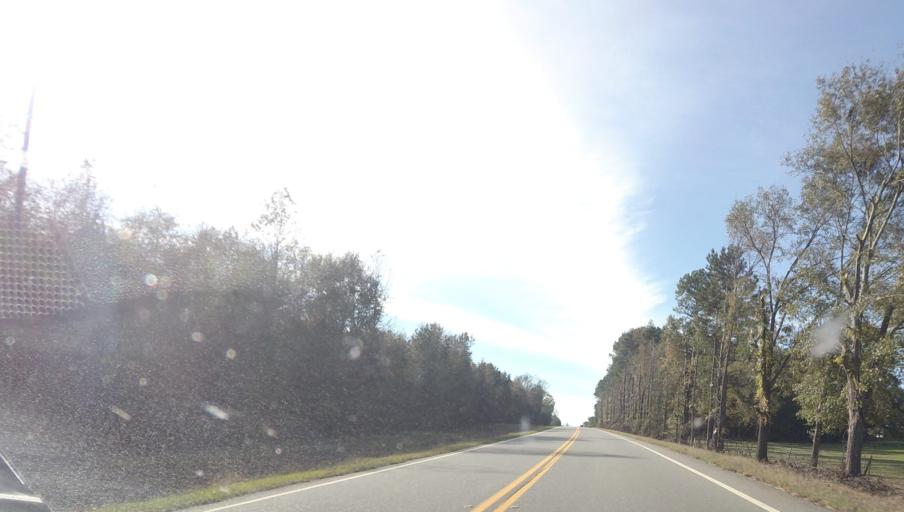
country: US
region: Georgia
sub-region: Upson County
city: Thomaston
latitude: 32.7204
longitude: -84.3146
